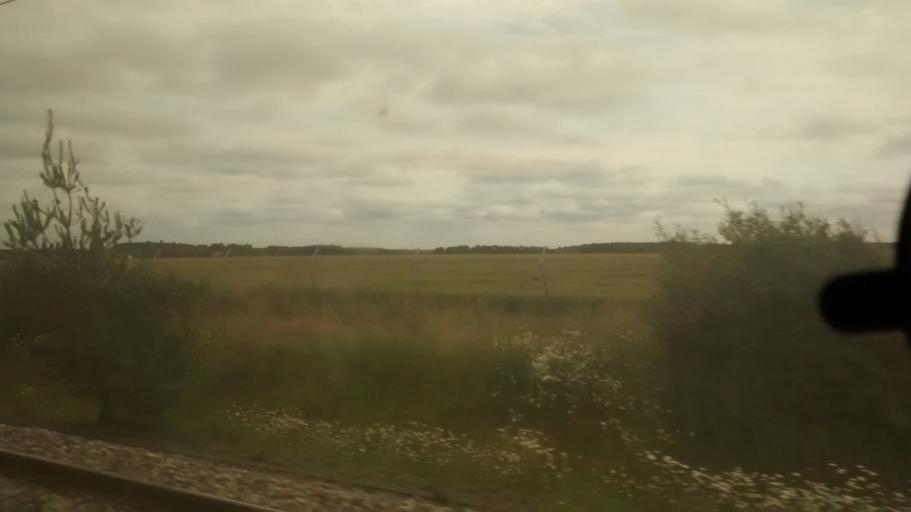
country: FR
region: Ile-de-France
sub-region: Departement de l'Essonne
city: Corbreuse
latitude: 48.5186
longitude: 1.9093
